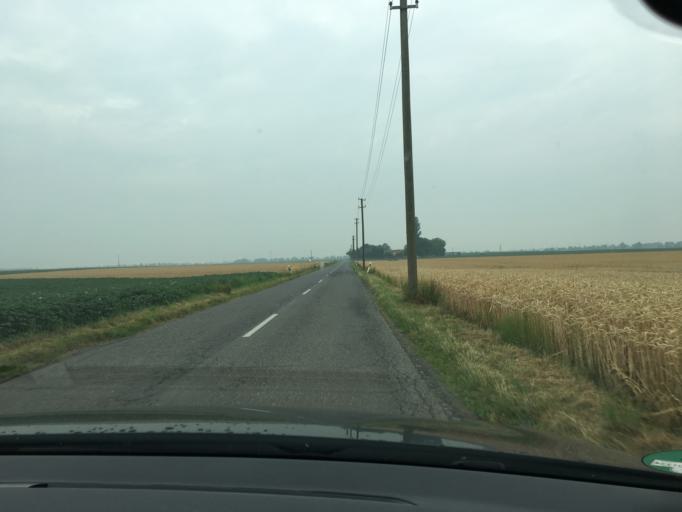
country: DE
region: North Rhine-Westphalia
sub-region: Regierungsbezirk Koln
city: Titz
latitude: 50.9779
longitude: 6.4046
